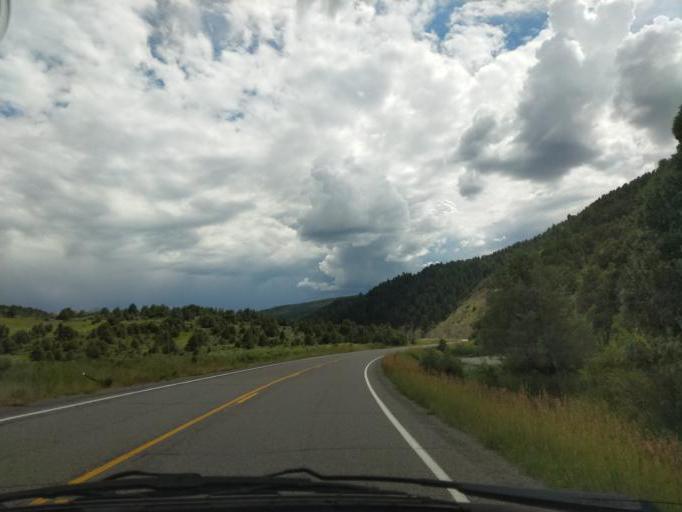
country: US
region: Colorado
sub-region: Delta County
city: Paonia
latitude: 39.0139
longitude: -107.3607
